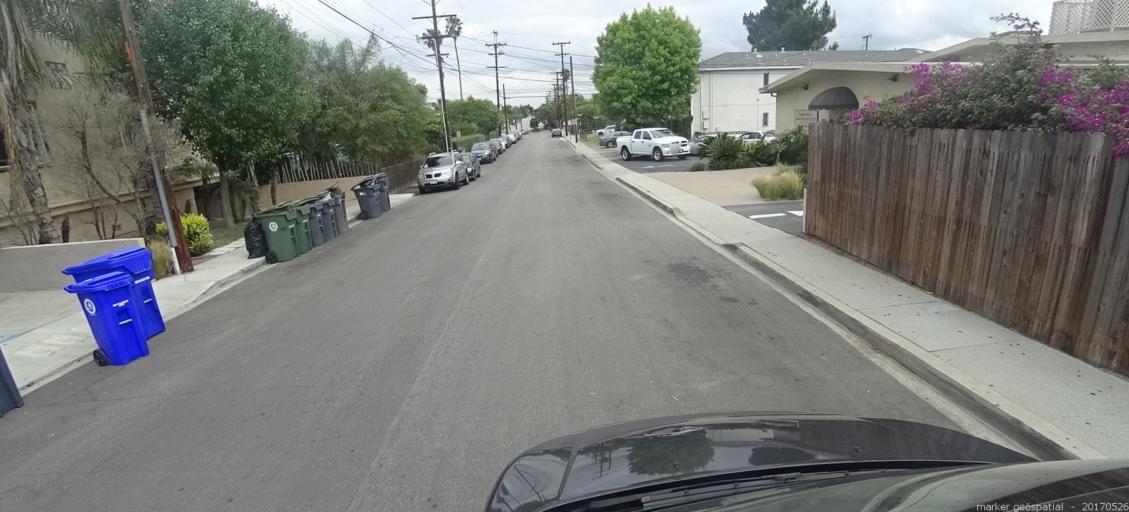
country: US
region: California
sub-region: Los Angeles County
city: Hermosa Beach
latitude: 33.8739
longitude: -118.3800
